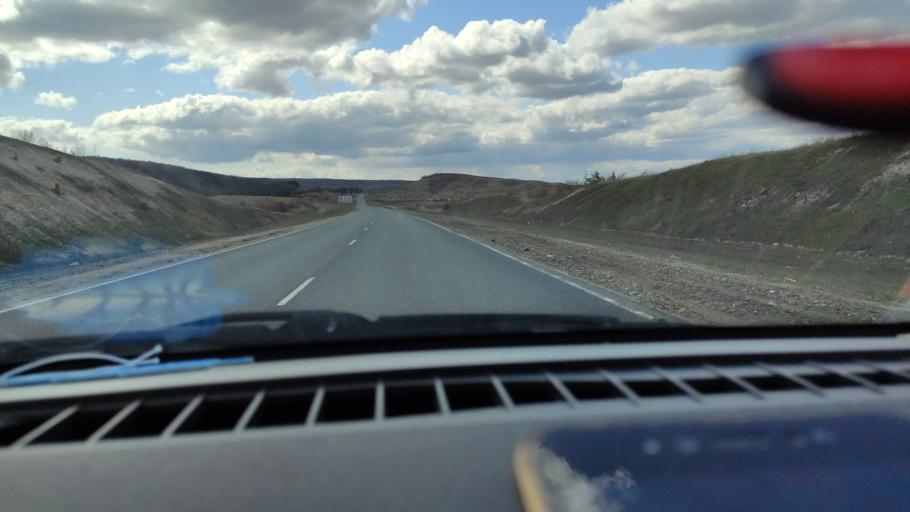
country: RU
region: Saratov
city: Alekseyevka
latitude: 52.3795
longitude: 47.9722
